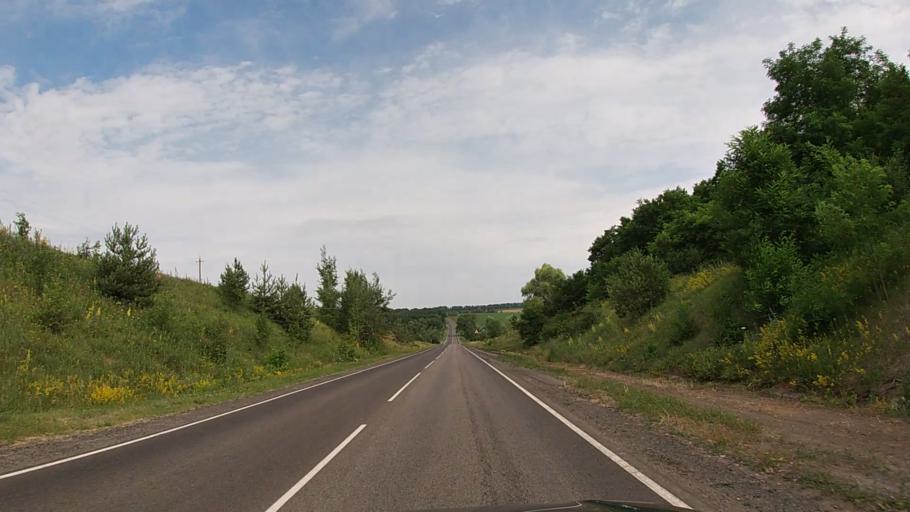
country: RU
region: Belgorod
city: Krasnaya Yaruga
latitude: 50.8244
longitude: 35.4996
